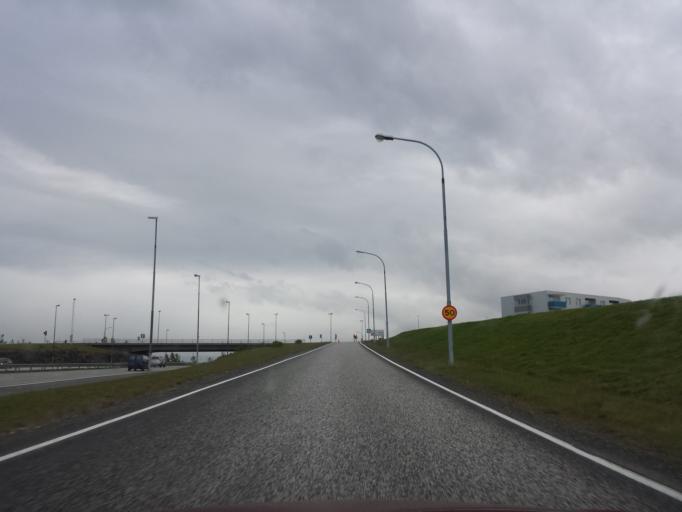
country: IS
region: Capital Region
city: Gardabaer
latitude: 64.0983
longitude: -21.9181
